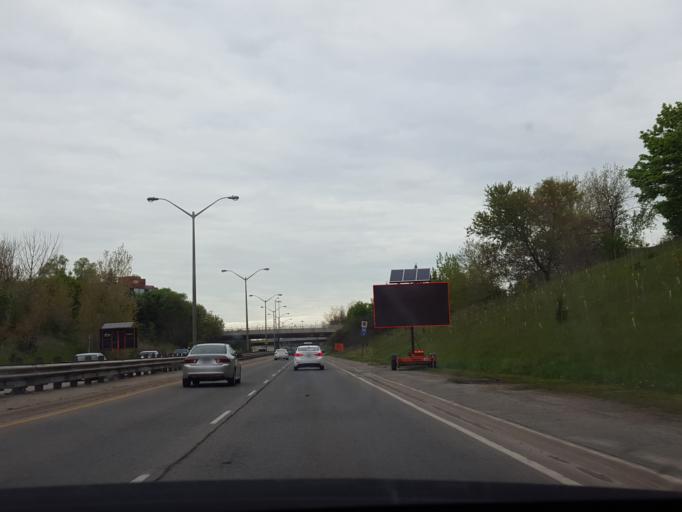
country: CA
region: Ontario
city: Toronto
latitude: 43.7072
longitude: -79.4969
